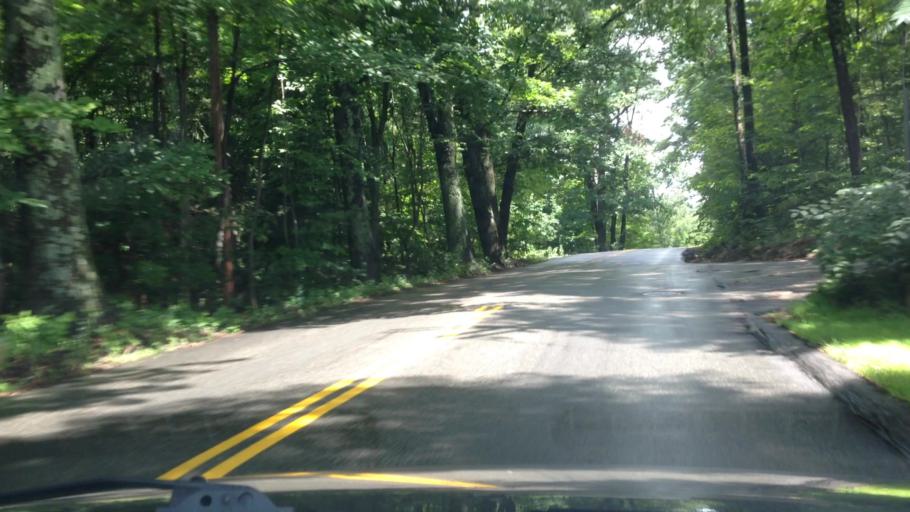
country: US
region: New Hampshire
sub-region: Cheshire County
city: Keene
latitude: 42.9127
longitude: -72.2528
